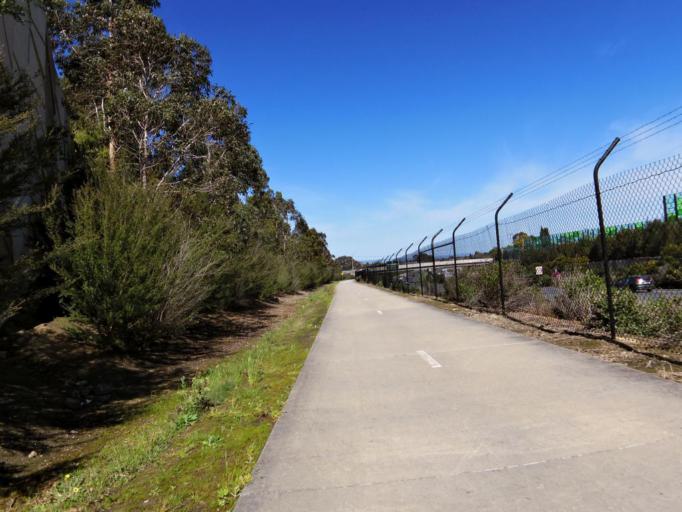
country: AU
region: Victoria
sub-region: Greater Dandenong
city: Noble Park North
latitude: -37.9538
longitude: 145.2035
